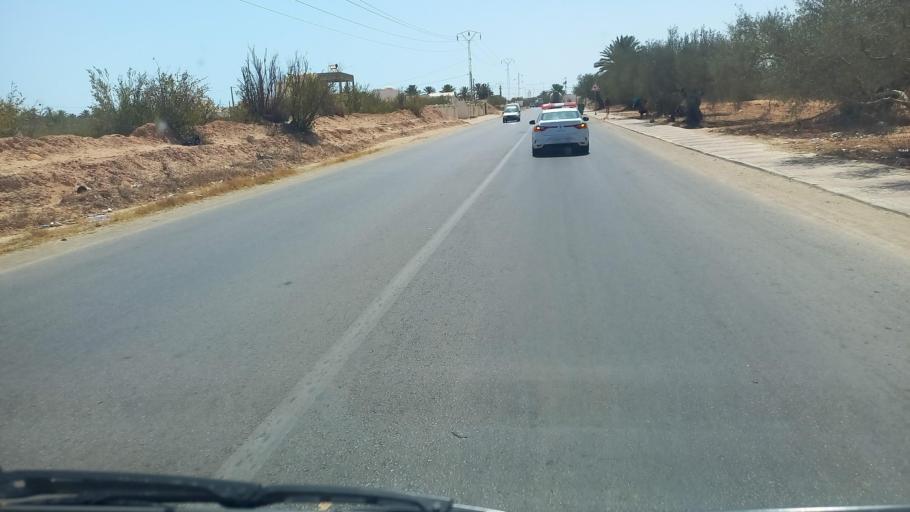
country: TN
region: Madanin
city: Midoun
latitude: 33.7729
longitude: 10.8974
